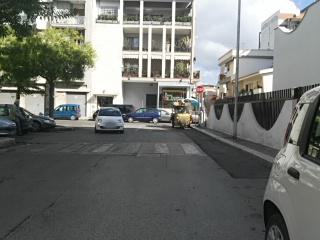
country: IT
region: Apulia
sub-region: Provincia di Bari
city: Triggiano
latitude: 41.0623
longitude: 16.9125
